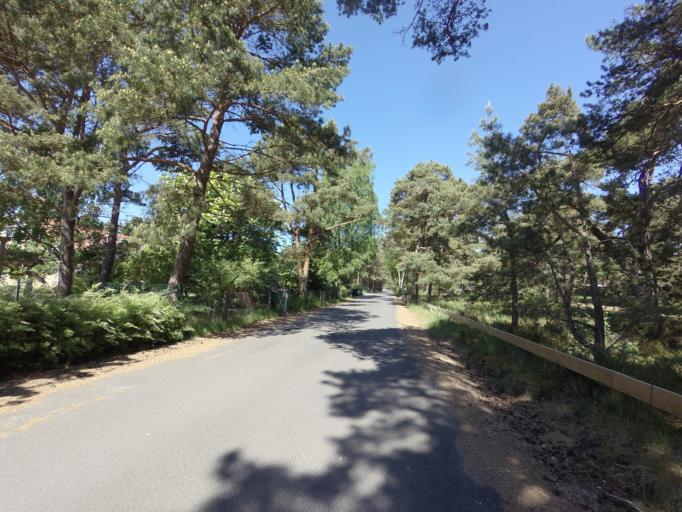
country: SE
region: Skane
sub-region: Vellinge Kommun
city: Hollviken
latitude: 55.4055
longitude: 12.9571
